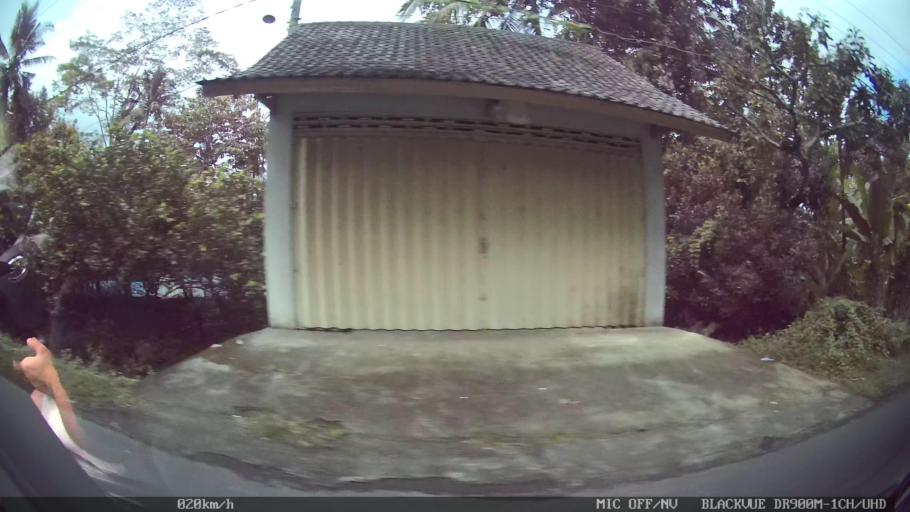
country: ID
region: Bali
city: Bangli
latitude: -8.4540
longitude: 115.3440
